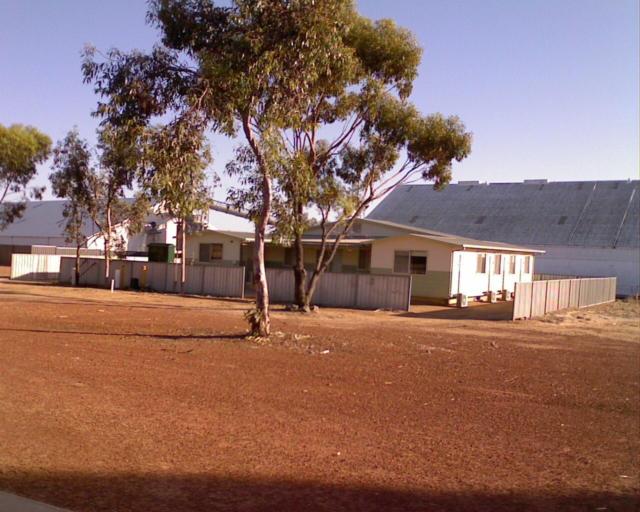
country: AU
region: Western Australia
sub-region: Wongan-Ballidu
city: Wongan Hills
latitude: -30.3606
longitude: 117.1156
